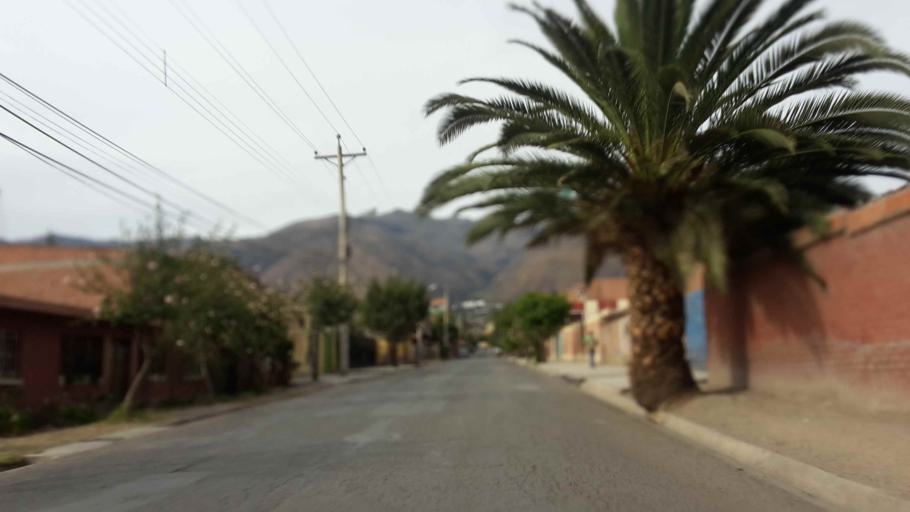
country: BO
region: Cochabamba
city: Cochabamba
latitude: -17.3560
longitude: -66.1950
